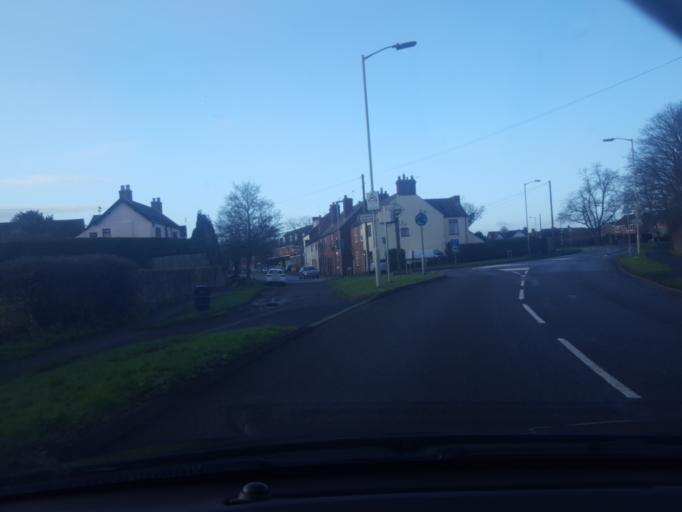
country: GB
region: England
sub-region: Staffordshire
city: Codsall
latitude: 52.6297
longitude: -2.1979
